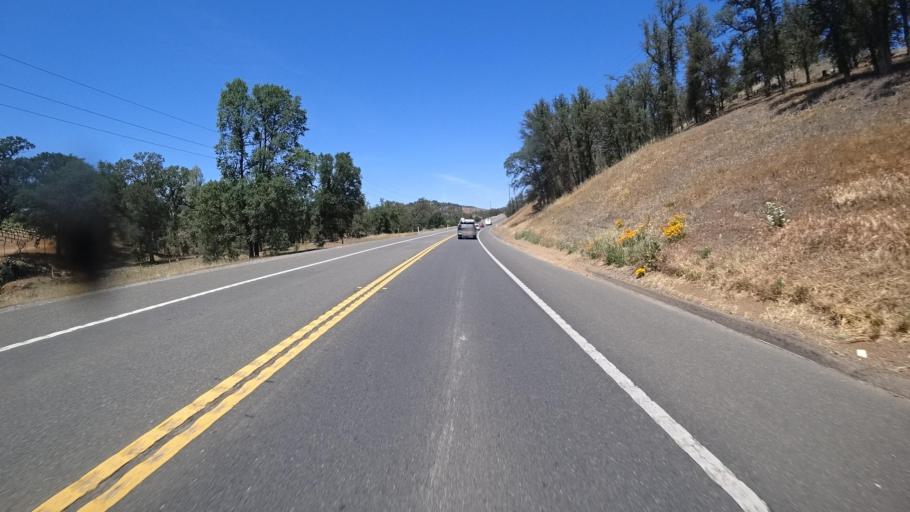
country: US
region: California
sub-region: Lake County
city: Clearlake
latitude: 38.9836
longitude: -122.6128
